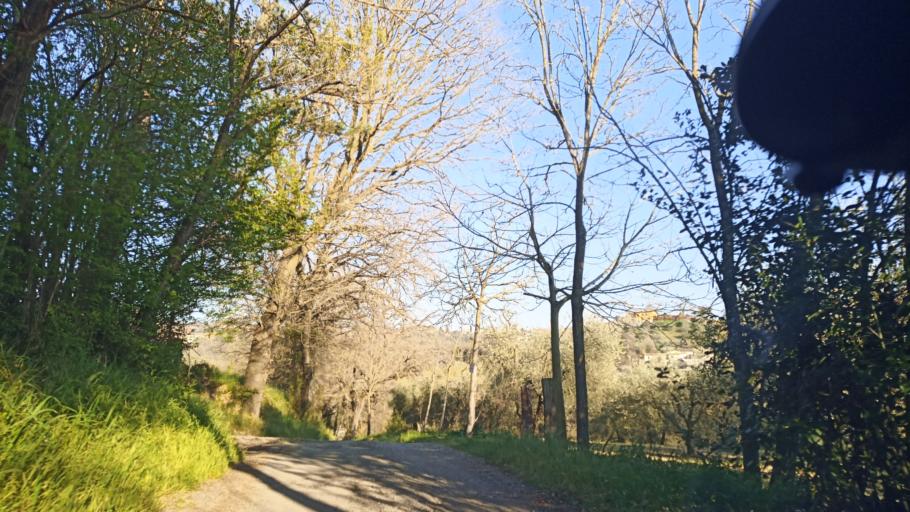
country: IT
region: Latium
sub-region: Provincia di Rieti
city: Poggio Mirteto
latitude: 42.2625
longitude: 12.6663
